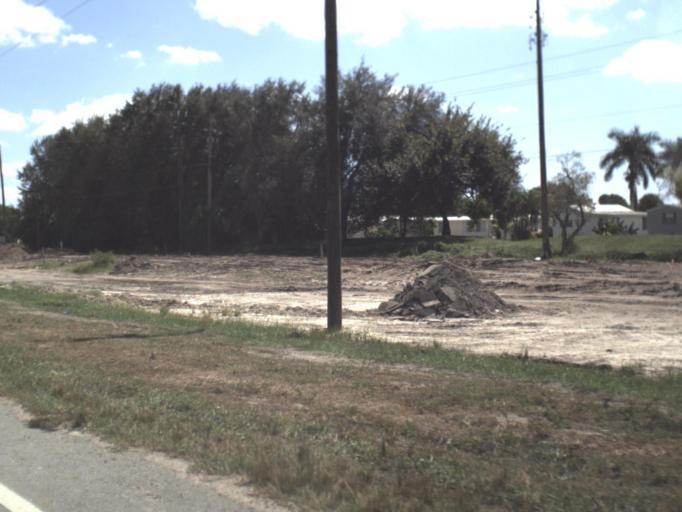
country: US
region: Florida
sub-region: Collier County
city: Lely Resort
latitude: 26.0435
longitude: -81.6681
